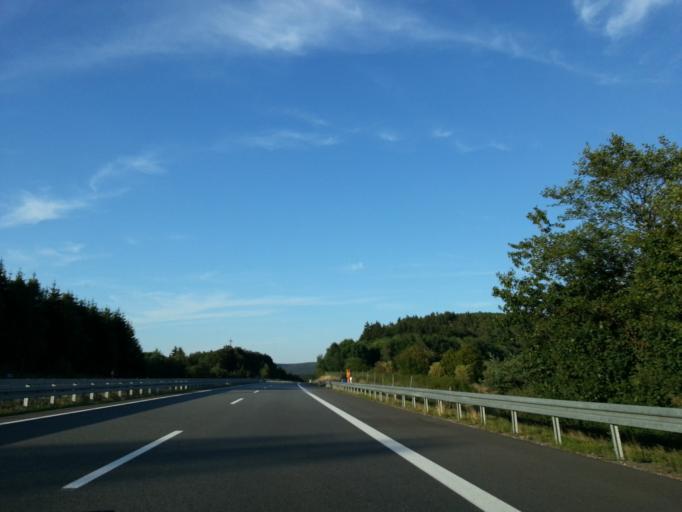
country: DE
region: Saarland
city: Nohfelden
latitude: 49.5930
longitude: 7.1274
